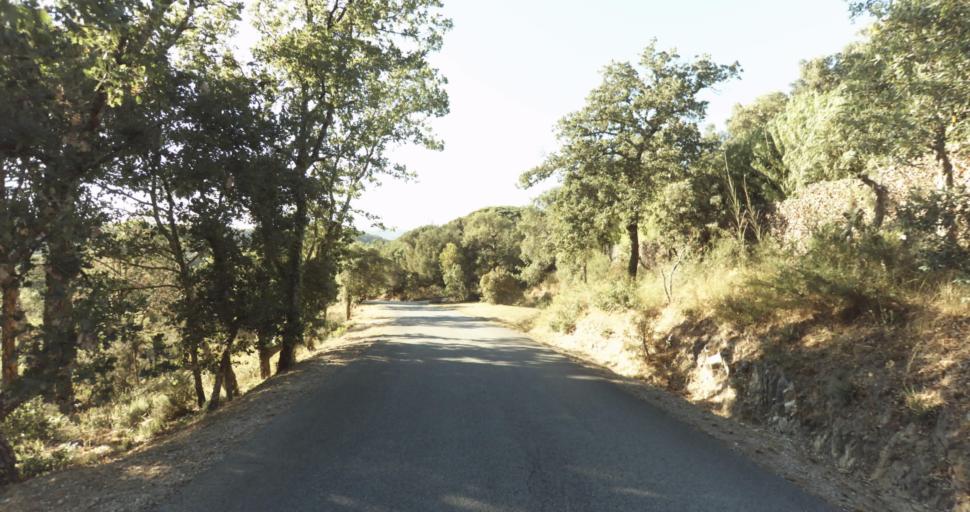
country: FR
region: Provence-Alpes-Cote d'Azur
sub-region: Departement du Var
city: Gassin
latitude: 43.2381
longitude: 6.5969
